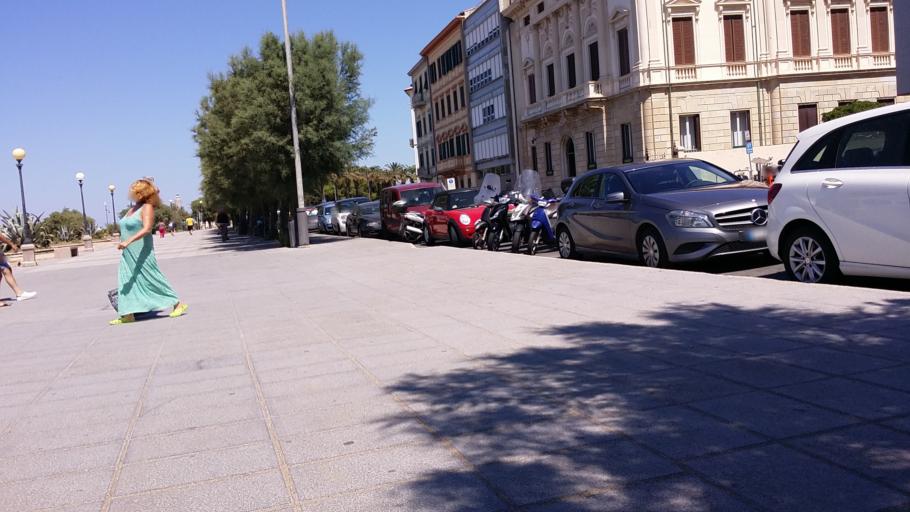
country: IT
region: Tuscany
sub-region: Provincia di Livorno
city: Livorno
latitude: 43.5333
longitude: 10.3019
